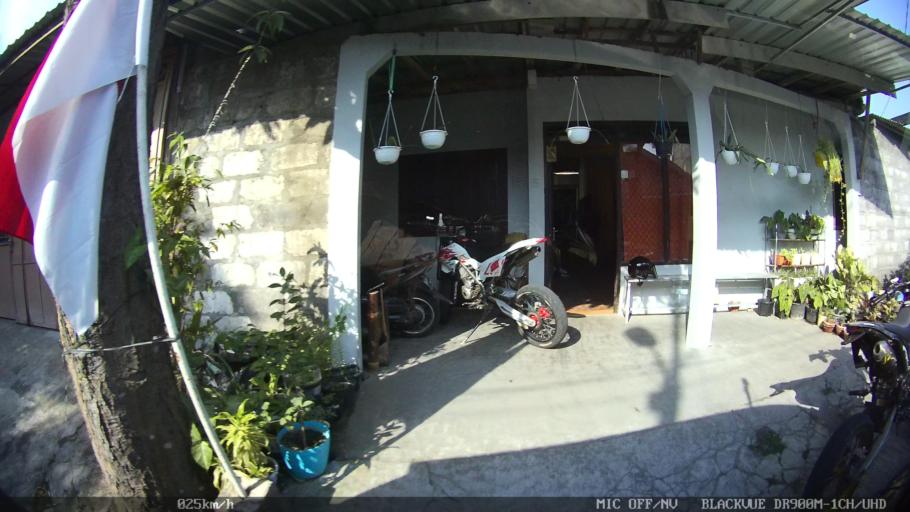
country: ID
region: Daerah Istimewa Yogyakarta
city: Yogyakarta
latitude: -7.8219
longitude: 110.3797
